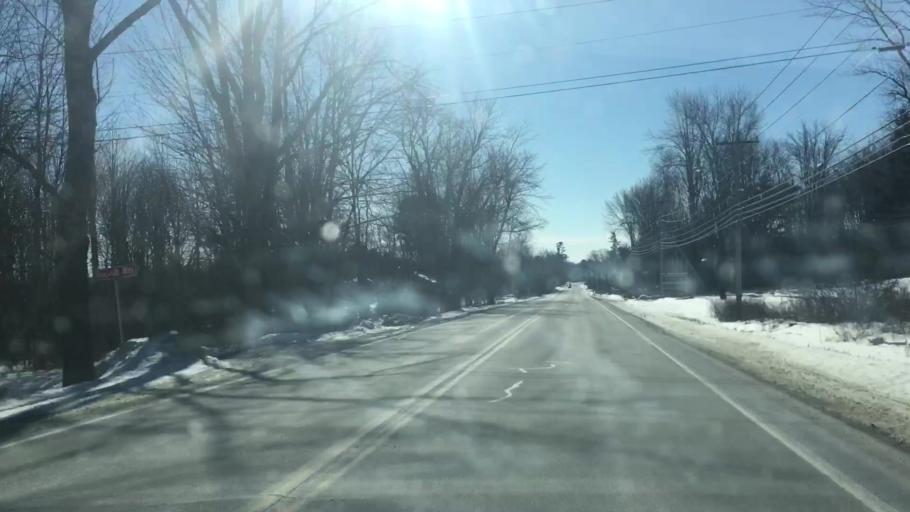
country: US
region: Maine
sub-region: Hancock County
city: Ellsworth
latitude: 44.5040
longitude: -68.4408
